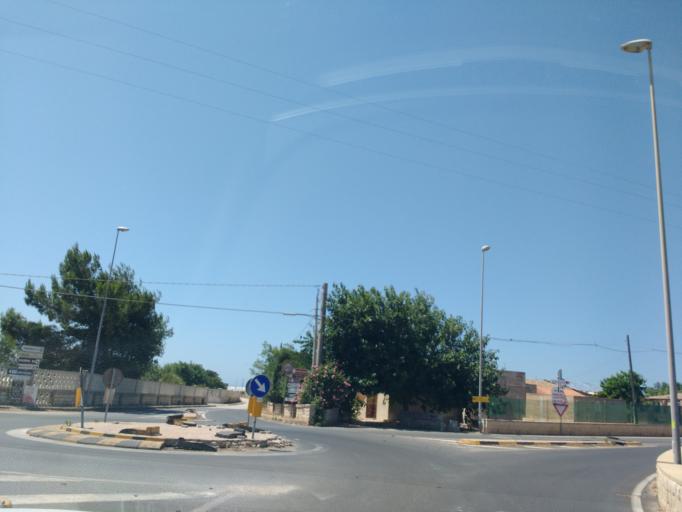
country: IT
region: Sicily
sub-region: Provincia di Siracusa
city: Portopalo di Capo Passero
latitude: 36.6730
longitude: 15.0952
